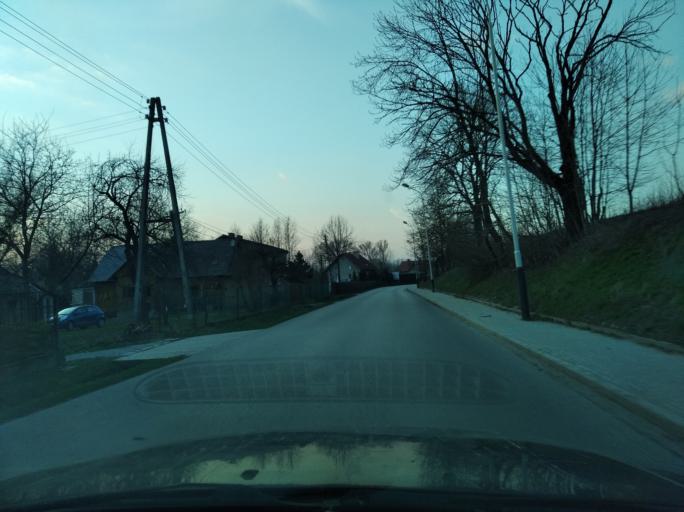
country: PL
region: Subcarpathian Voivodeship
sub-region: Powiat przeworski
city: Przeworsk
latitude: 50.0452
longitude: 22.5032
